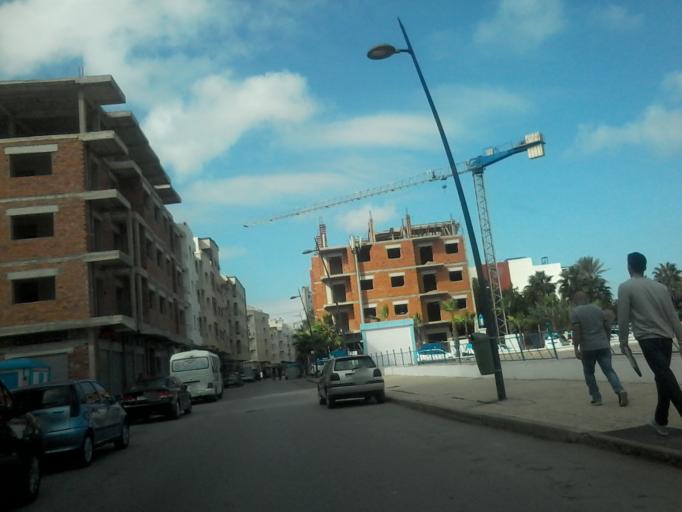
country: MA
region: Tanger-Tetouan
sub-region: Tetouan
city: Martil
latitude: 35.6857
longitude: -5.3240
